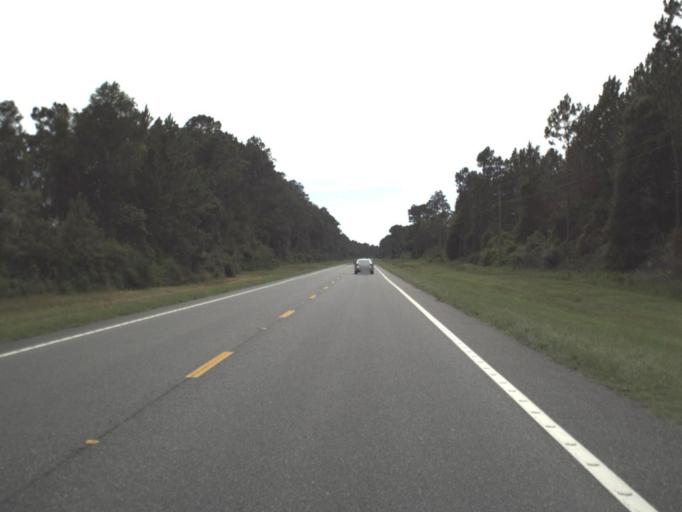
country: US
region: Florida
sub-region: Taylor County
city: Perry
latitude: 30.1074
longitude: -83.4278
